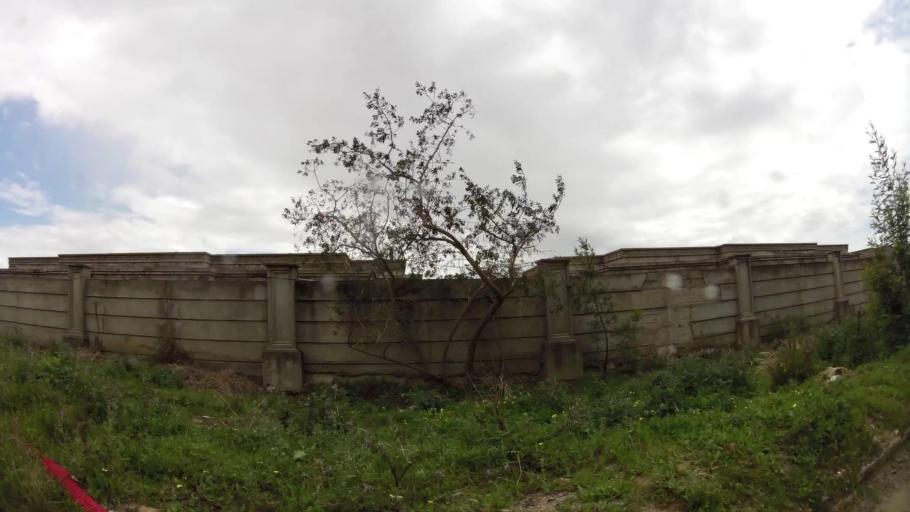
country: MA
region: Tanger-Tetouan
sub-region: Tanger-Assilah
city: Tangier
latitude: 35.7803
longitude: -5.8563
